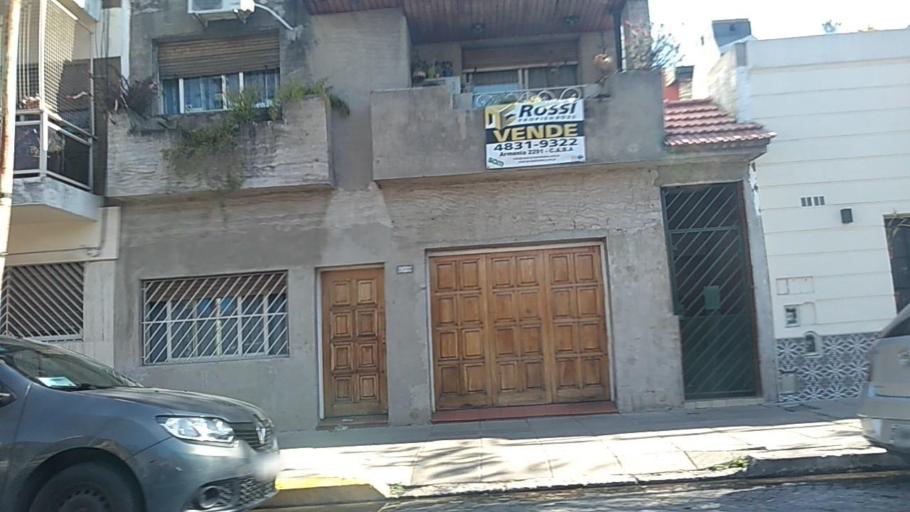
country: AR
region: Buenos Aires F.D.
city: Villa Santa Rita
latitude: -34.6101
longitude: -58.4944
